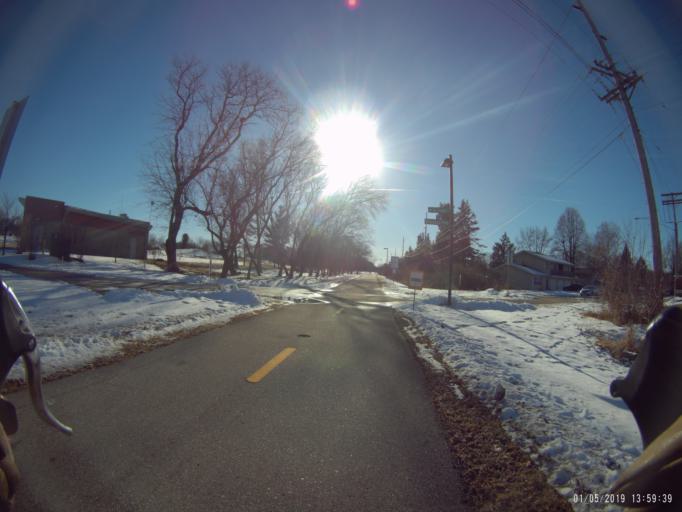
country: US
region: Wisconsin
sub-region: Dane County
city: Madison
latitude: 43.0315
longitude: -89.4198
